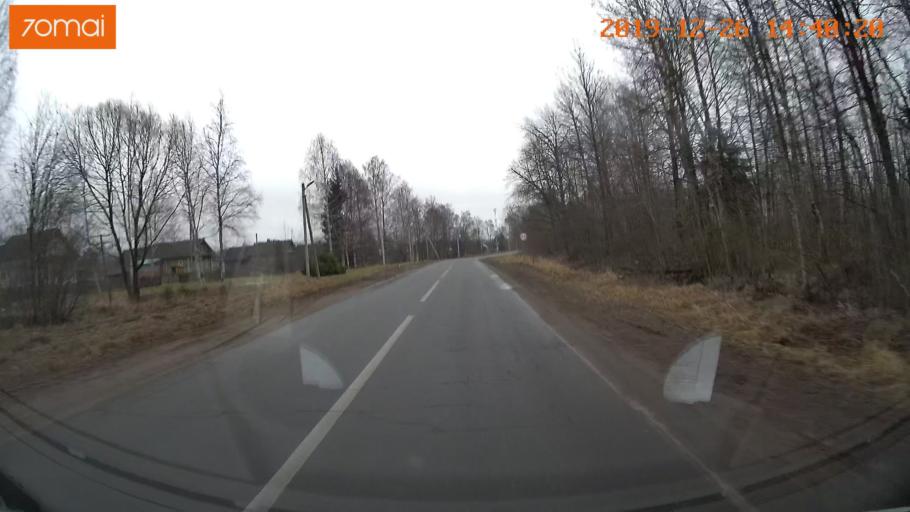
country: RU
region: Jaroslavl
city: Poshekhon'ye
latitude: 58.3766
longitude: 38.9970
